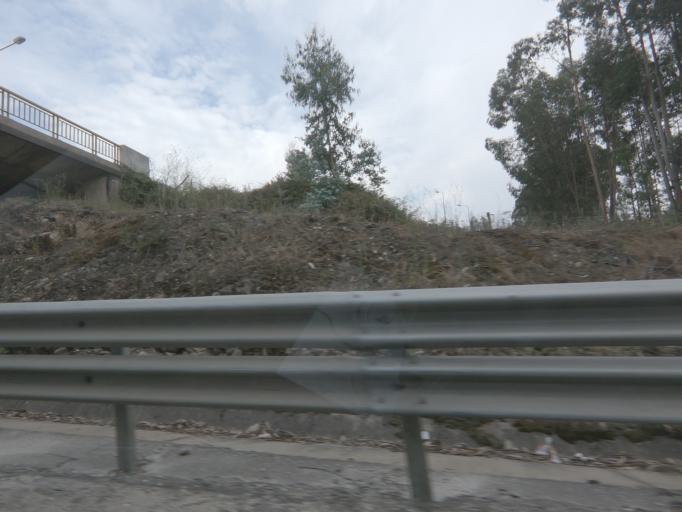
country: PT
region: Coimbra
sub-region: Penacova
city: Lorvao
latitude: 40.3029
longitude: -8.3482
